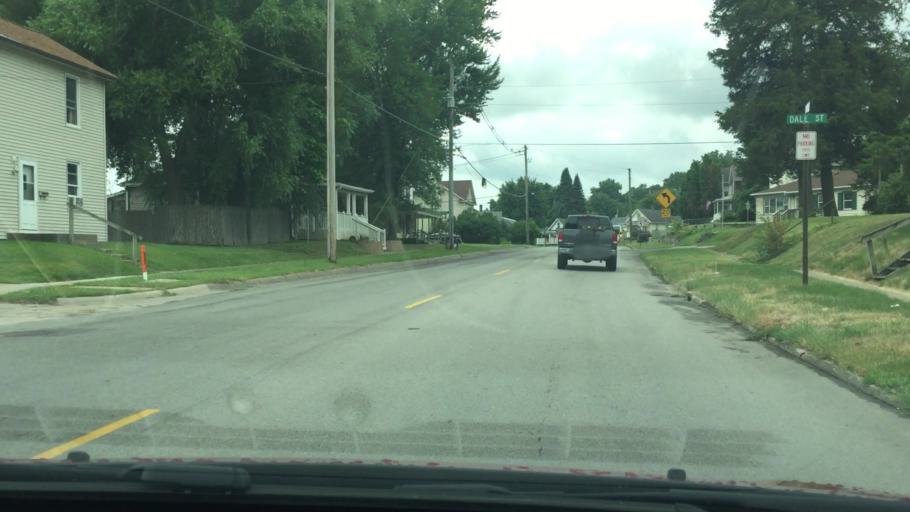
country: US
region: Iowa
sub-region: Muscatine County
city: Muscatine
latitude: 41.4351
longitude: -91.0428
